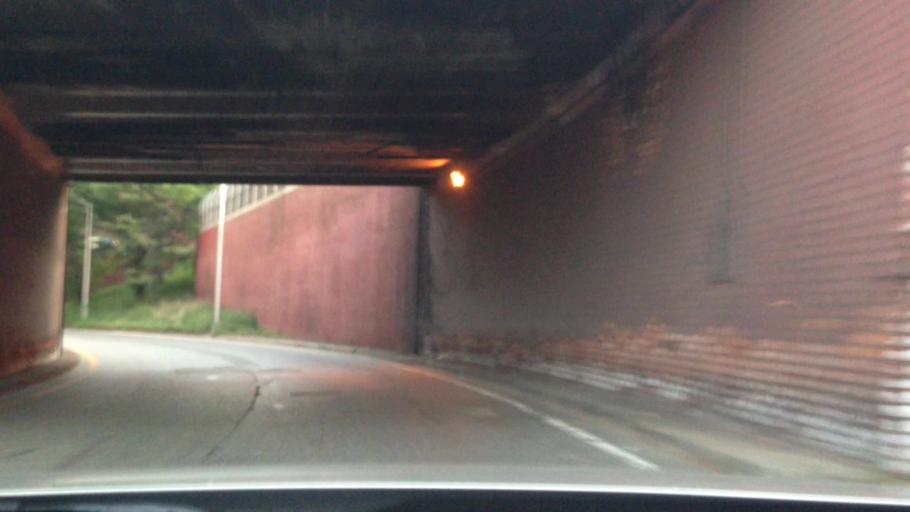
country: US
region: New York
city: New York City
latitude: 40.6801
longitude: -74.0021
